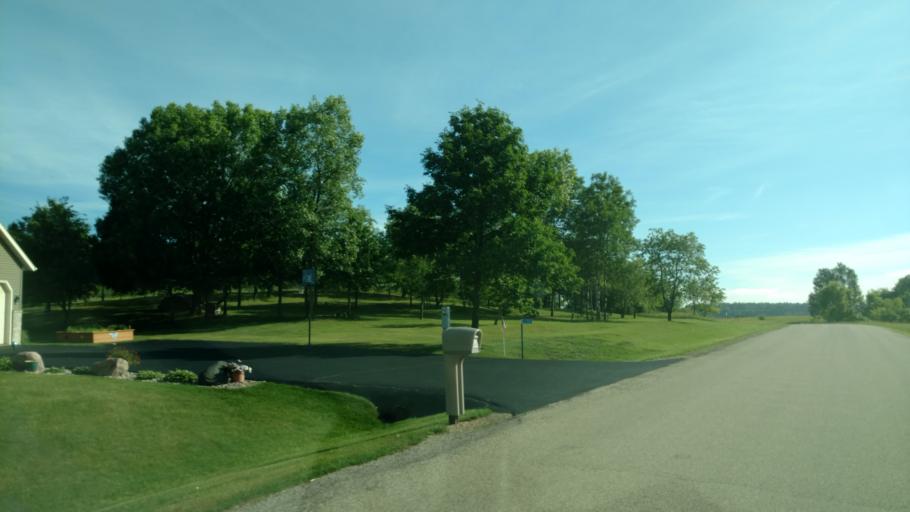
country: US
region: Wisconsin
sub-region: Vernon County
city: Hillsboro
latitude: 43.5873
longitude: -90.1817
